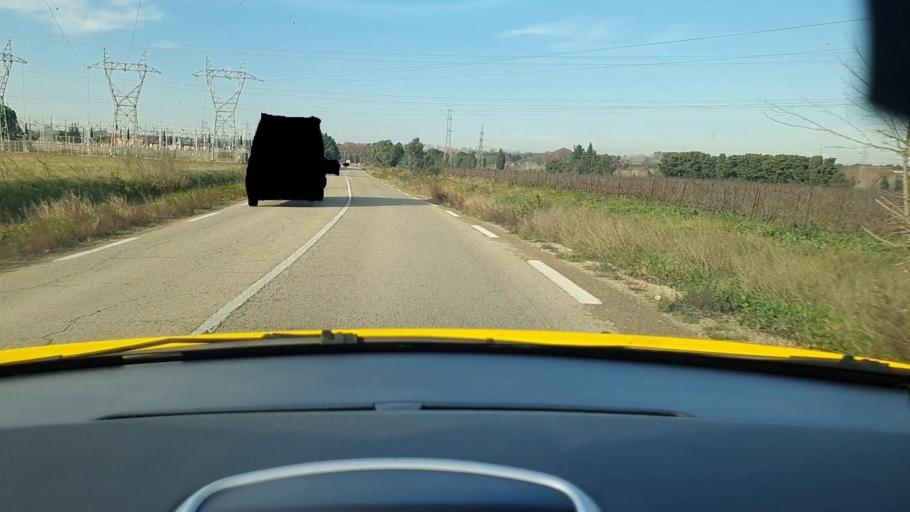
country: FR
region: Languedoc-Roussillon
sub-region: Departement du Gard
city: Jonquieres-Saint-Vincent
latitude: 43.8296
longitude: 4.5888
